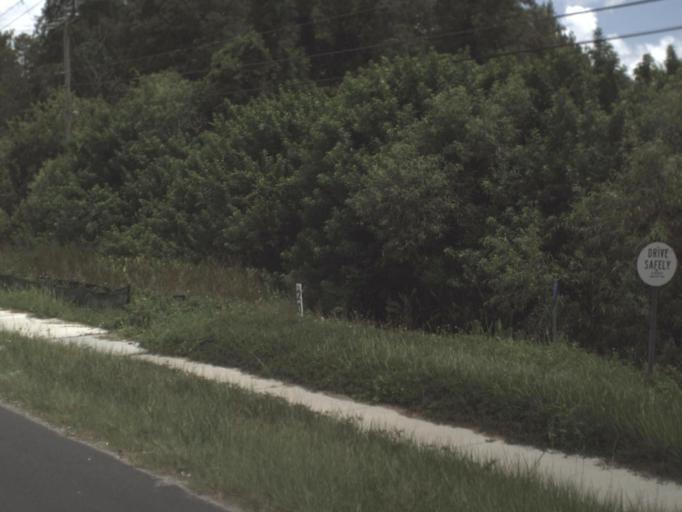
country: US
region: Florida
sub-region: Hillsborough County
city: Egypt Lake-Leto
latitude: 27.9961
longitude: -82.5216
